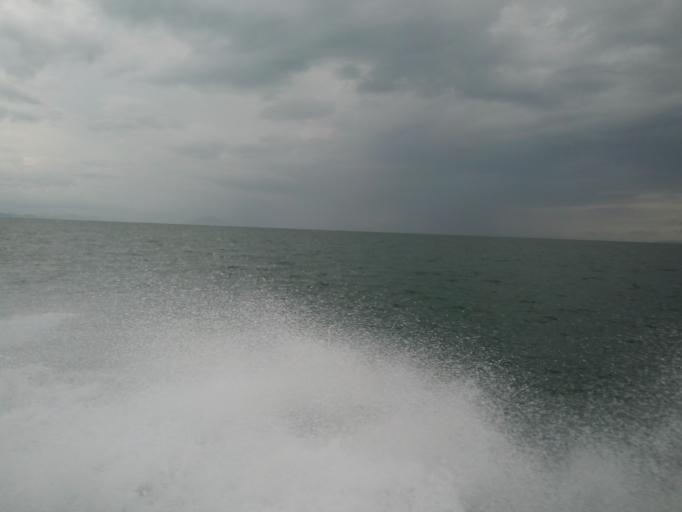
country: TH
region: Phangnga
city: Ban Ao Nang
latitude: 8.0115
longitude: 98.8581
